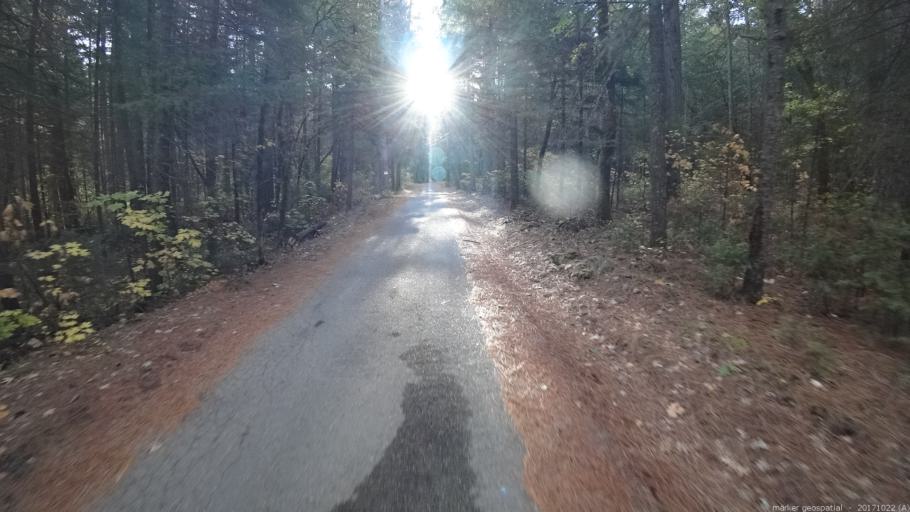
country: US
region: California
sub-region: Siskiyou County
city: Dunsmuir
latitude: 41.1711
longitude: -122.2726
